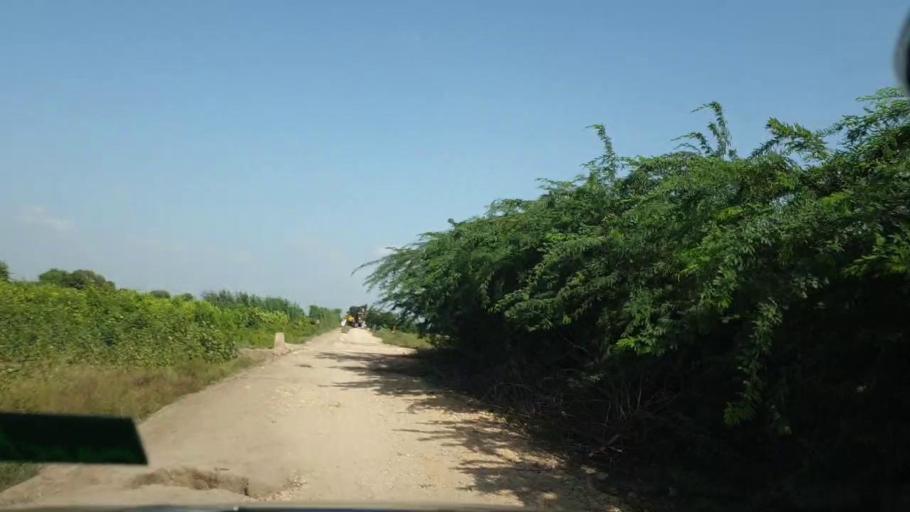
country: PK
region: Sindh
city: Naukot
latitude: 24.7030
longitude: 69.2282
